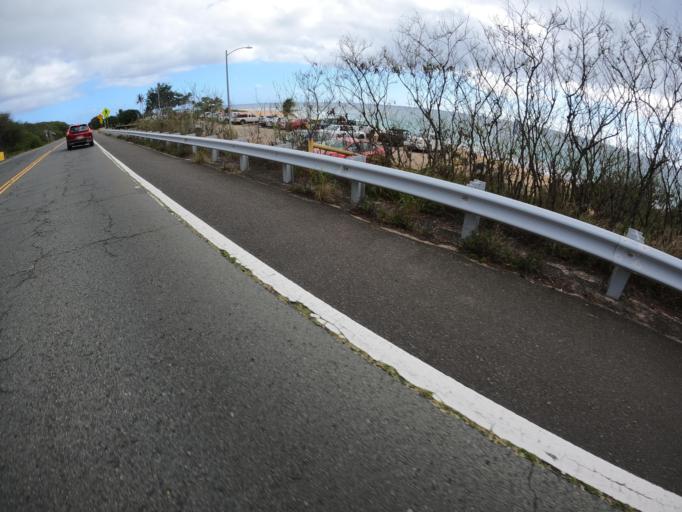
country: US
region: Hawaii
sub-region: Honolulu County
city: Waimanalo Beach
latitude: 21.2859
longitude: -157.6744
